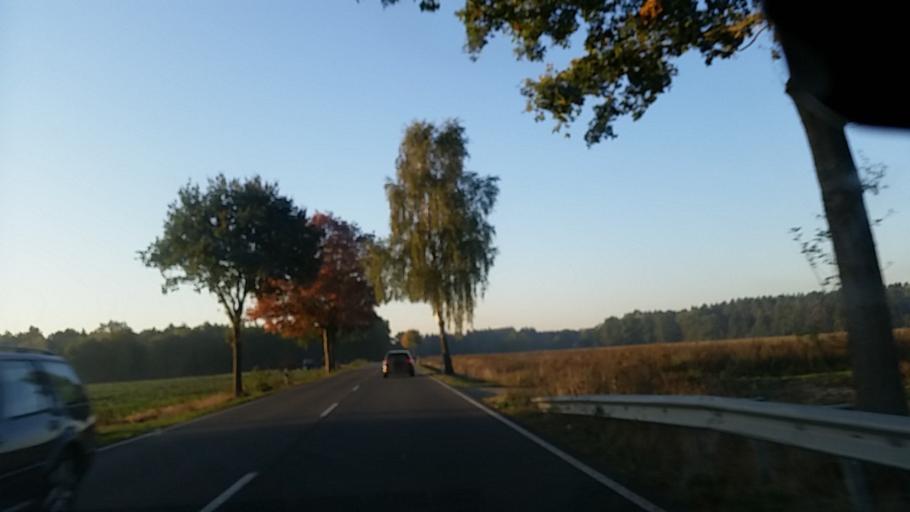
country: DE
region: Lower Saxony
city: Barwedel
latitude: 52.5517
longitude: 10.7859
